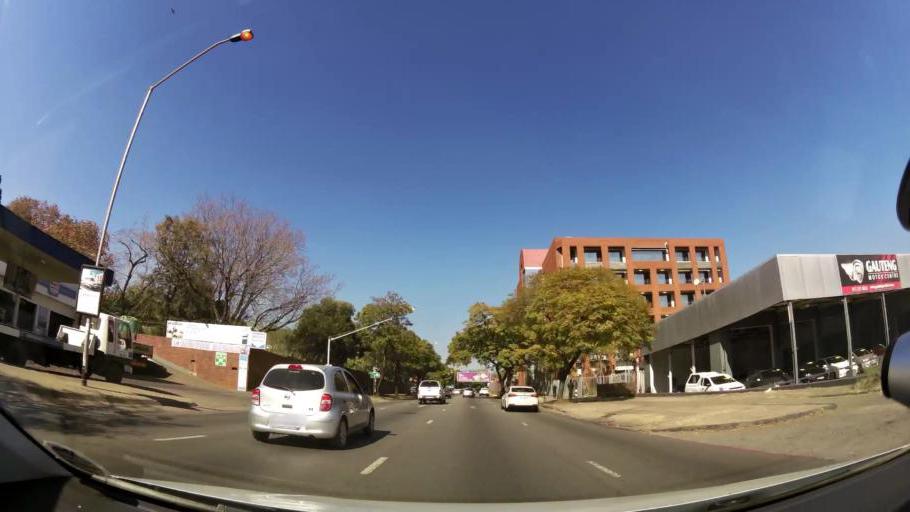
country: ZA
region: Gauteng
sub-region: City of Tshwane Metropolitan Municipality
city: Pretoria
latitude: -25.7517
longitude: 28.1836
